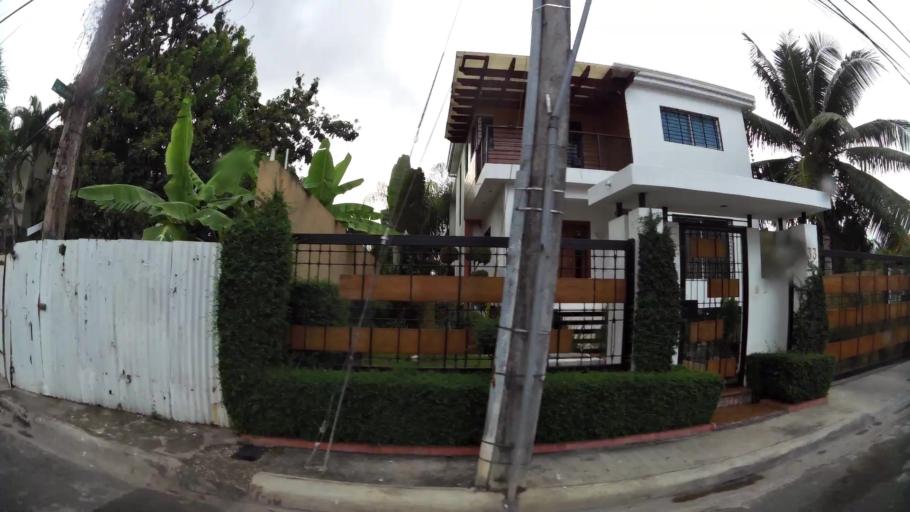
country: DO
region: Nacional
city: Santo Domingo
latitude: 18.5002
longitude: -69.9719
